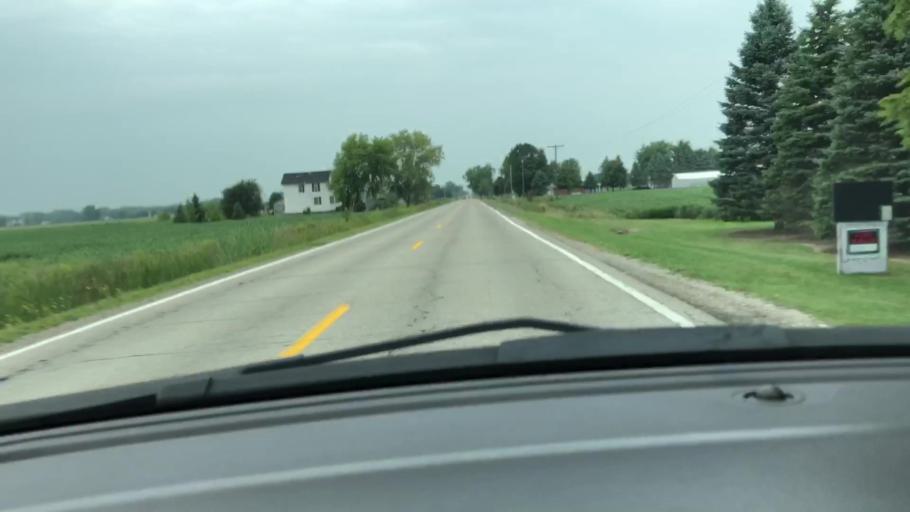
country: US
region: Michigan
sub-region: Bay County
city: Auburn
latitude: 43.5719
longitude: -84.0897
